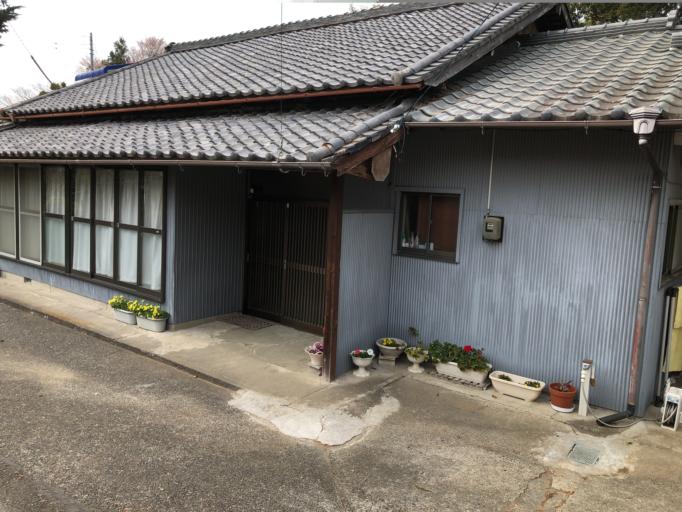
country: JP
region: Shizuoka
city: Kanaya
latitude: 34.8040
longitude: 138.0804
